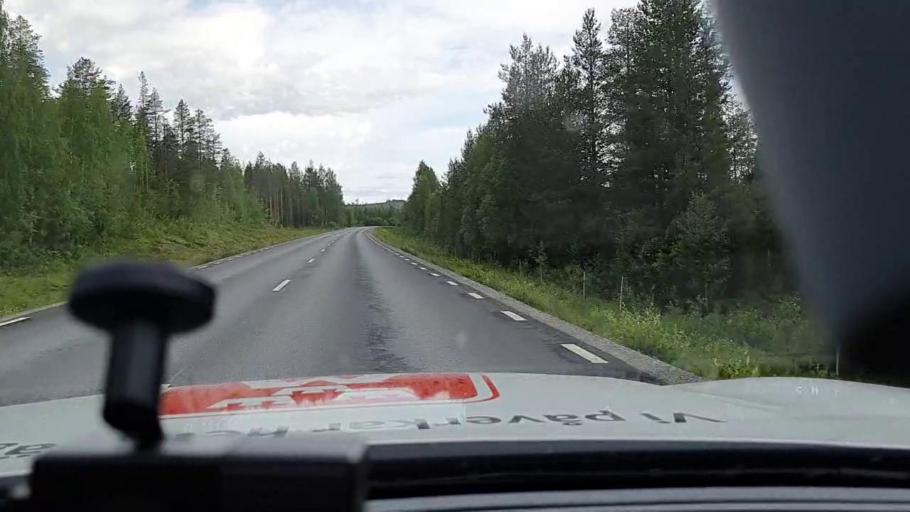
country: SE
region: Norrbotten
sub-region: Gallivare Kommun
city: Gaellivare
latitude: 66.4245
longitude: 20.6137
